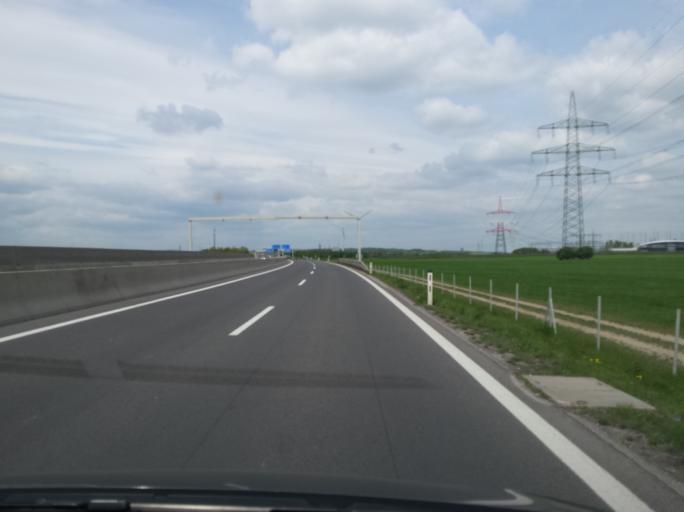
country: AT
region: Lower Austria
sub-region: Politischer Bezirk Wien-Umgebung
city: Leopoldsdorf
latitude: 48.1144
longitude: 16.4148
